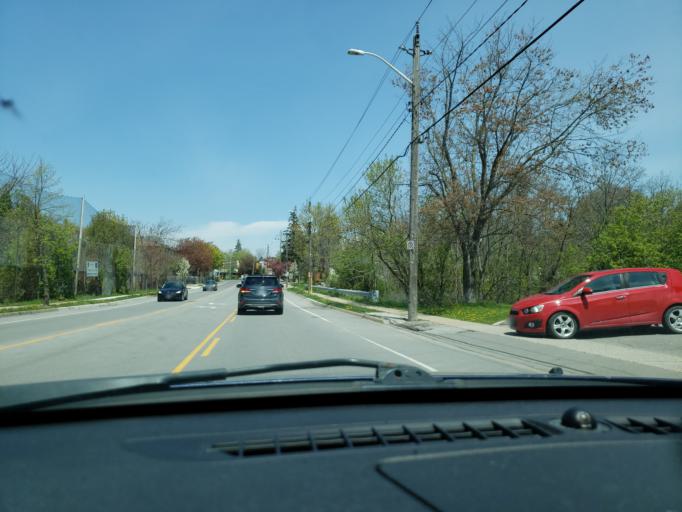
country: CA
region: Ontario
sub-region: Regional Municipality of Niagara
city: St. Catharines
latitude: 43.1570
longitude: -79.2144
